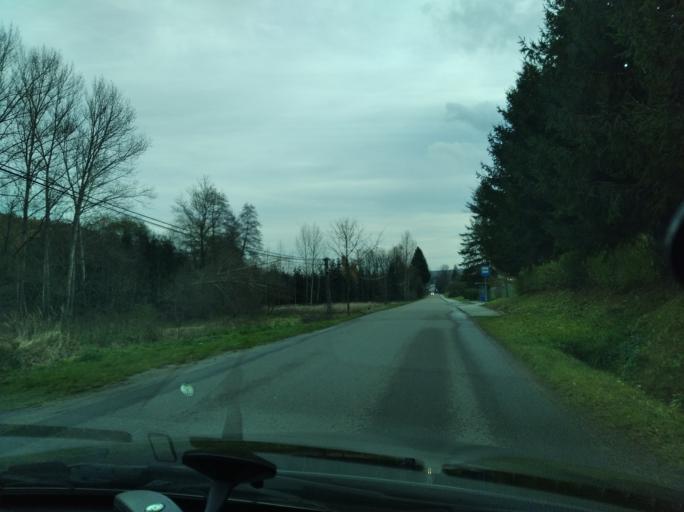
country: PL
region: Subcarpathian Voivodeship
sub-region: Powiat strzyzowski
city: Strzyzow
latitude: 49.9402
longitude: 21.7549
